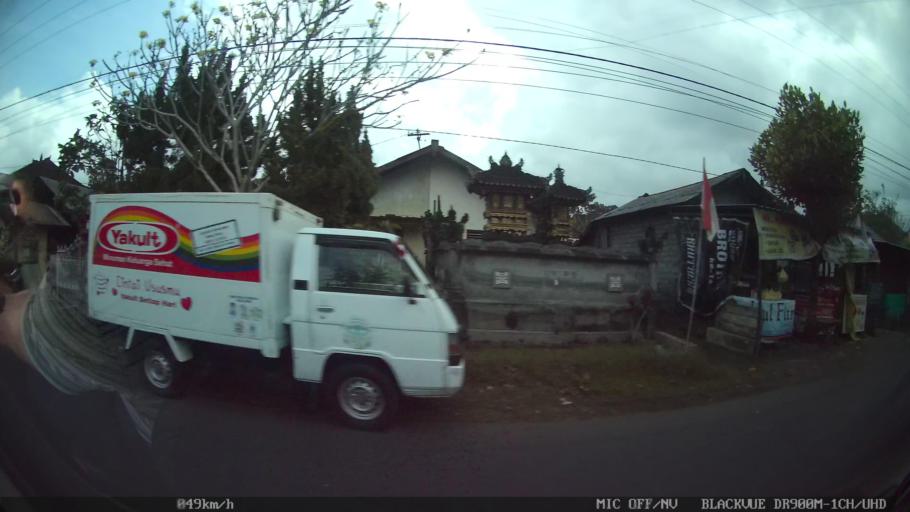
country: ID
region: Bali
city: Pohgending Kawan
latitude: -8.4567
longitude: 115.1385
